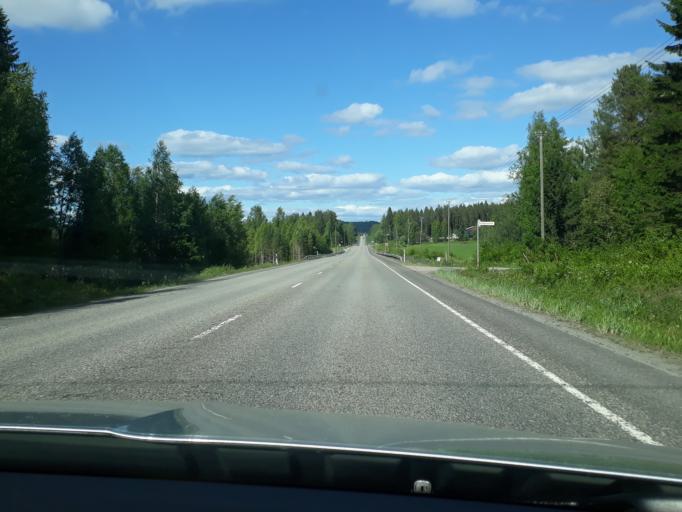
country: FI
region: Central Finland
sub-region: AEaenekoski
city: AEaenekoski
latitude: 62.6525
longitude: 25.7199
